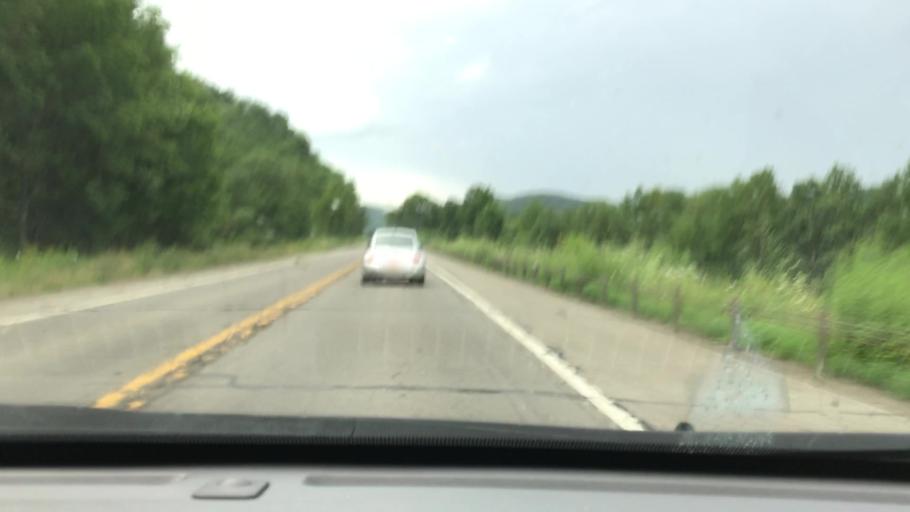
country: US
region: New York
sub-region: Cattaraugus County
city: Salamanca
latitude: 42.2371
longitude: -78.6399
